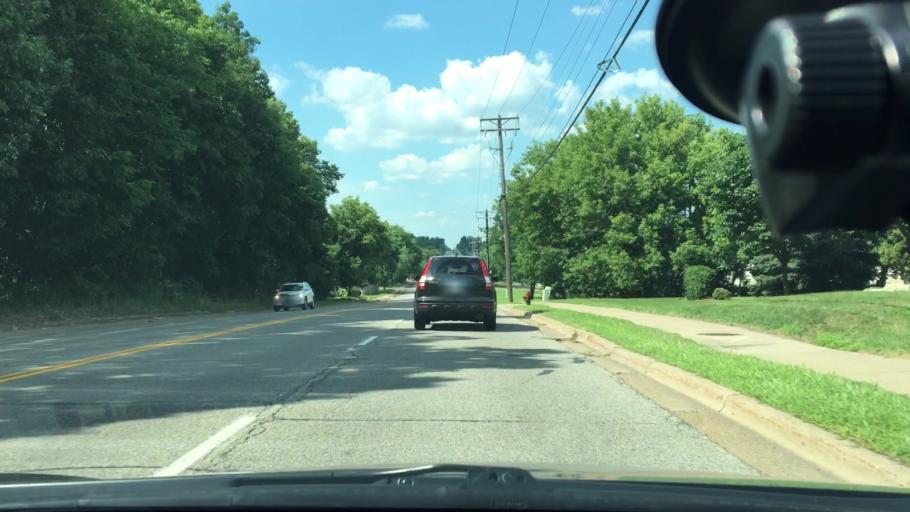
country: US
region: Minnesota
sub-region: Hennepin County
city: New Hope
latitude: 45.0179
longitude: -93.3802
